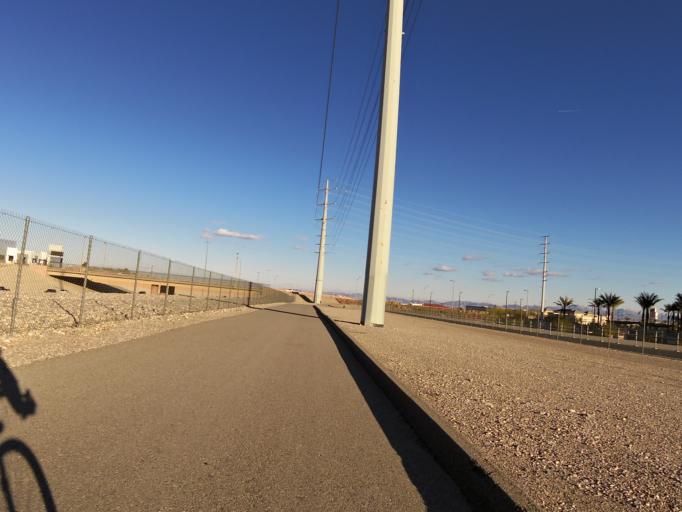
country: US
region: Nevada
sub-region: Clark County
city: Summerlin South
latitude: 36.1187
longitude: -115.3173
